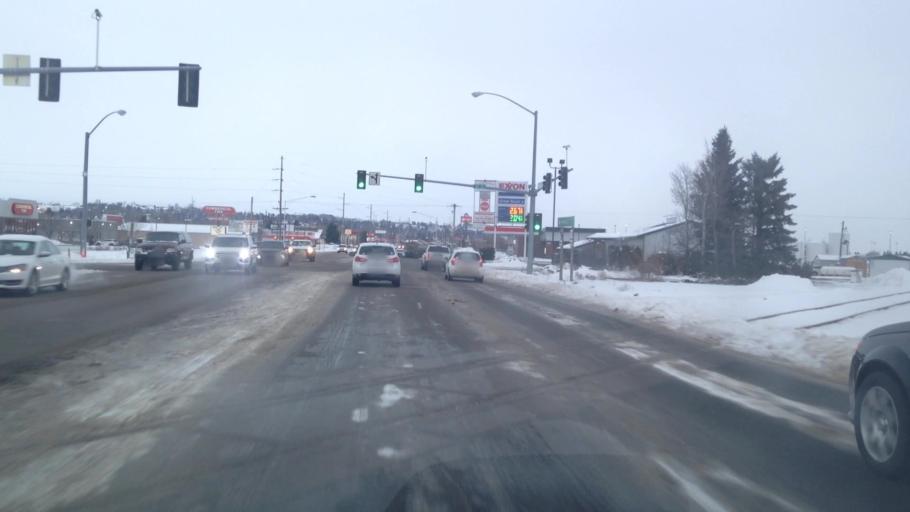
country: US
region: Idaho
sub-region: Madison County
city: Rexburg
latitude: 43.8420
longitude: -111.7783
